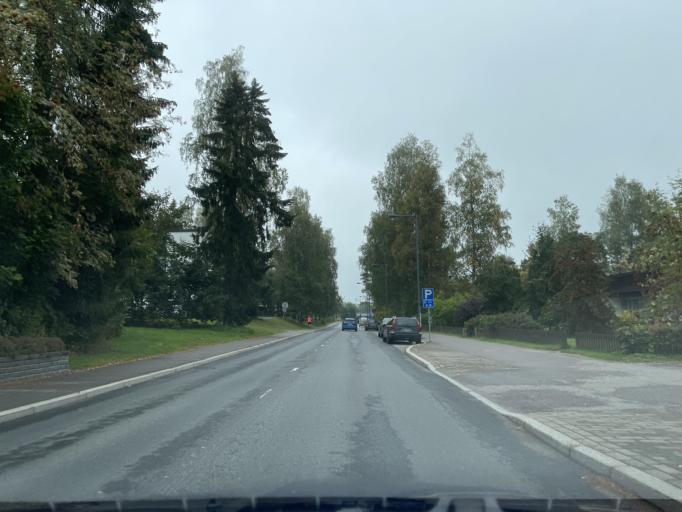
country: FI
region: Uusimaa
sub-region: Helsinki
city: Hyvinge
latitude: 60.6260
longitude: 24.8589
